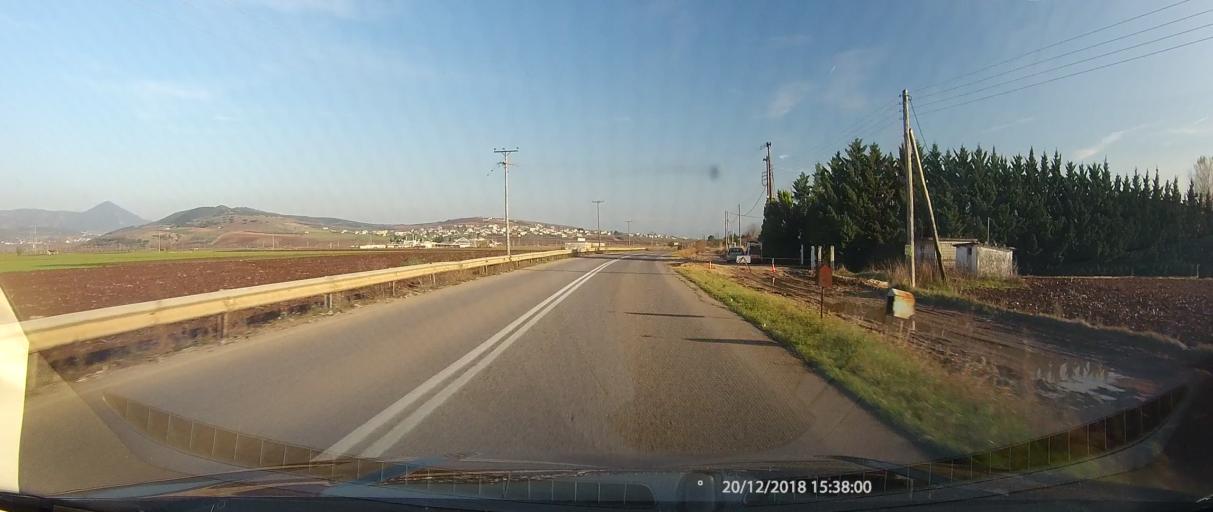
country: GR
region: Central Greece
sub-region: Nomos Fthiotidos
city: Stavros
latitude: 38.9076
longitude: 22.3417
